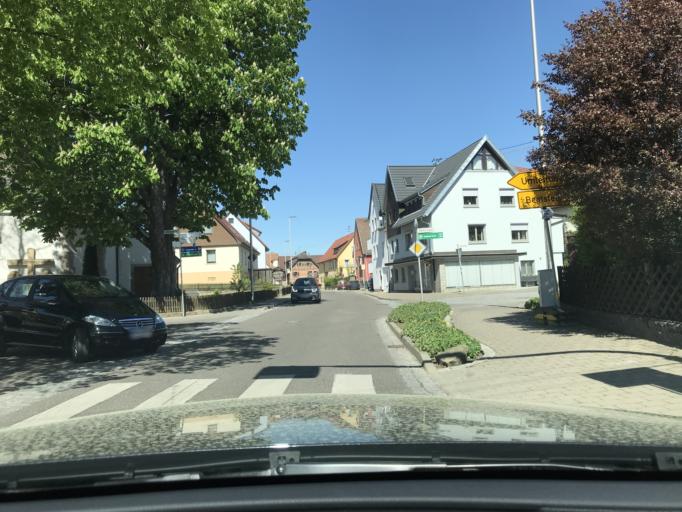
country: DE
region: Baden-Wuerttemberg
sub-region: Regierungsbezirk Stuttgart
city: Korb
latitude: 48.8290
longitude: 9.3752
